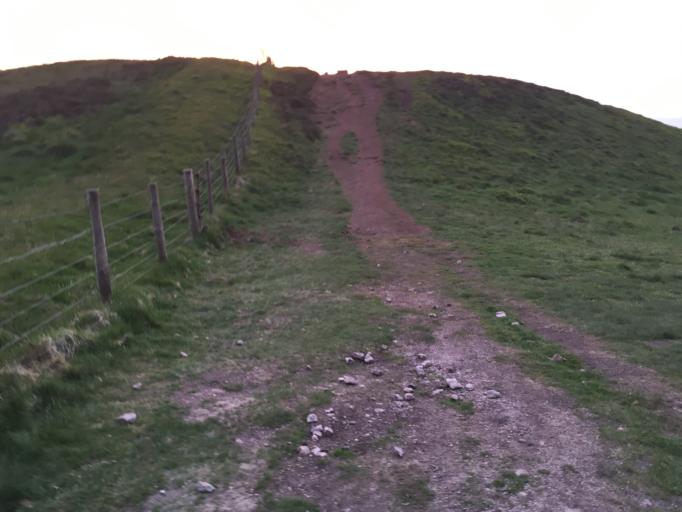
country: GB
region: Scotland
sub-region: Edinburgh
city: Colinton
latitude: 55.8828
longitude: -3.2252
